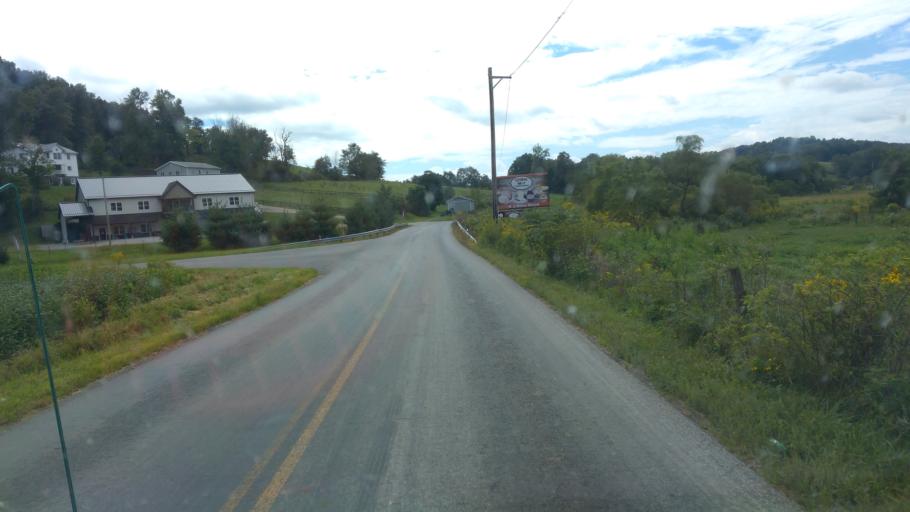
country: US
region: Ohio
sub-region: Holmes County
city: Millersburg
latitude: 40.5364
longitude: -81.8063
